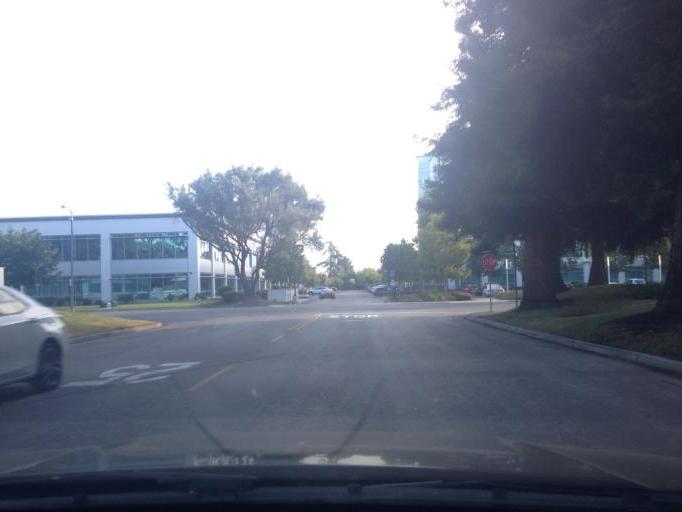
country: US
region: California
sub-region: Santa Clara County
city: Sunnyvale
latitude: 37.3968
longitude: -122.0310
